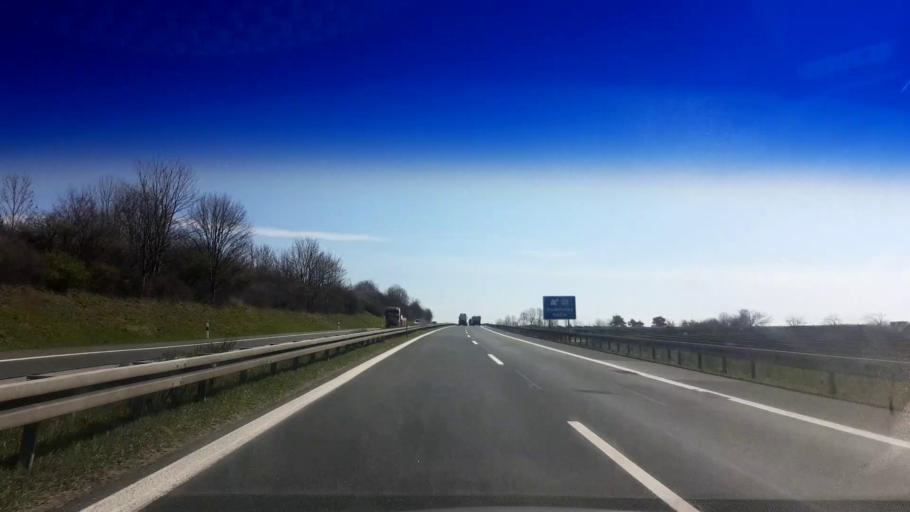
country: DE
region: Bavaria
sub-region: Upper Franconia
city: Stadelhofen
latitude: 49.9976
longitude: 11.1908
